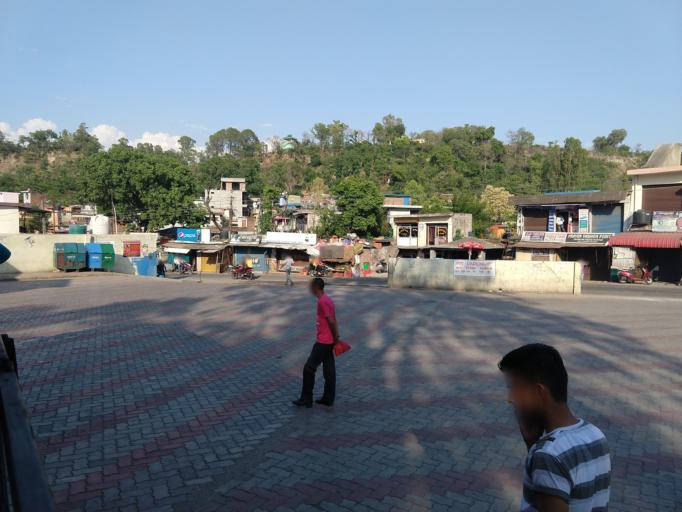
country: IN
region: Punjab
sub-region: Gurdaspur
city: Dharkalan
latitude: 32.3033
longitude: 75.8931
